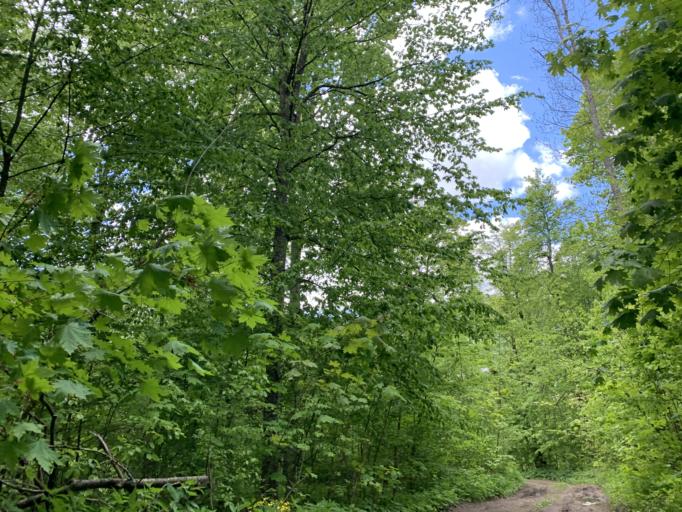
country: BY
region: Minsk
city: Nyasvizh
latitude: 53.1928
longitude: 26.6496
